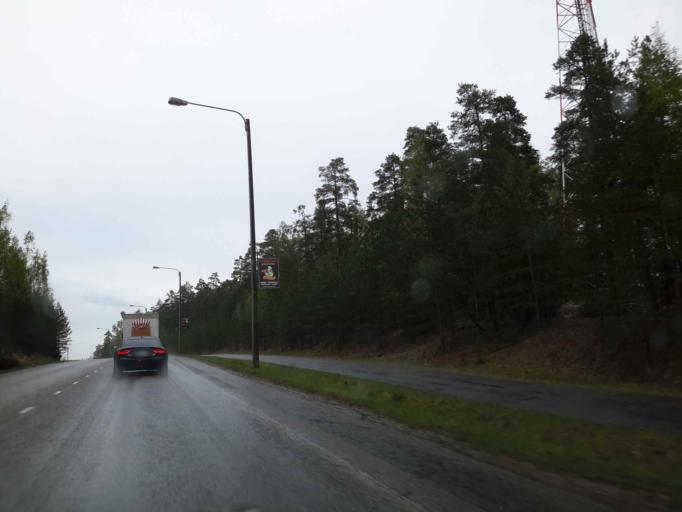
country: FI
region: Uusimaa
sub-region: Helsinki
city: Vihti
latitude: 60.3448
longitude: 24.3214
